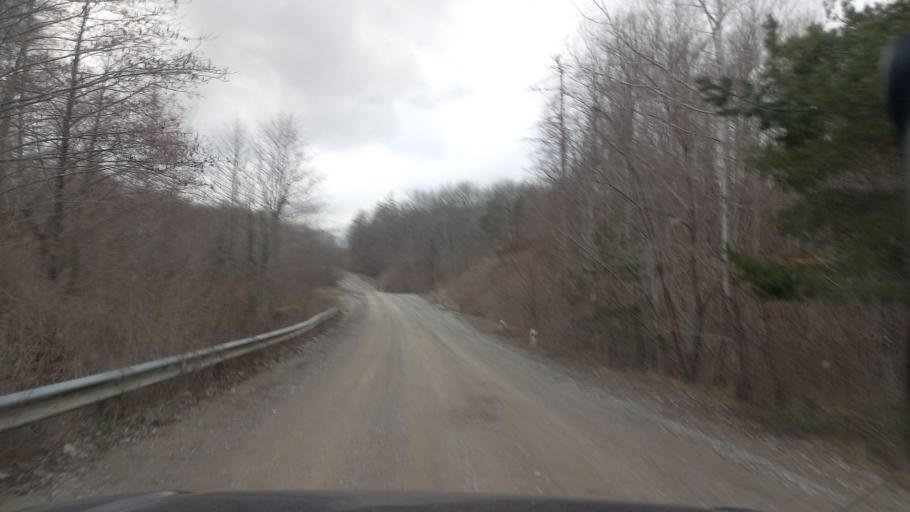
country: RU
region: Krasnodarskiy
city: Dzhubga
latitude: 44.5392
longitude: 38.7851
